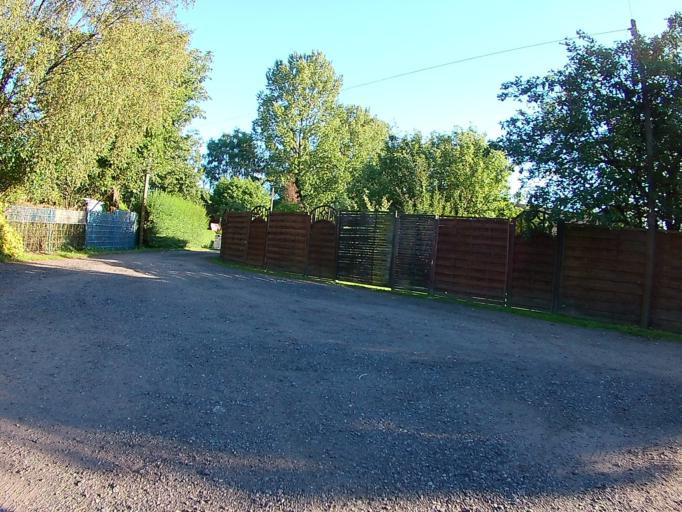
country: DE
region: Hamburg
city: Harburg
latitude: 53.4673
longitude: 9.9987
